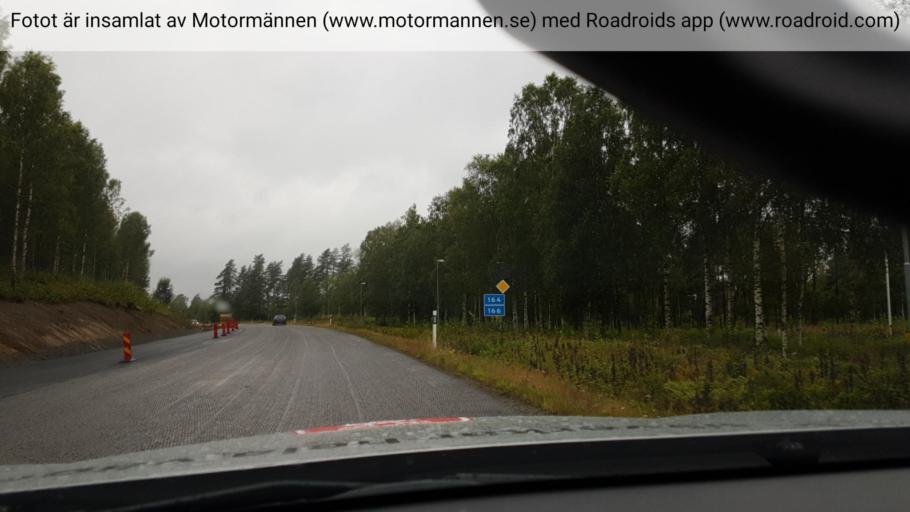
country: SE
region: Vaestra Goetaland
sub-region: Dals-Ed Kommun
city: Ed
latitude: 58.9004
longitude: 11.9437
